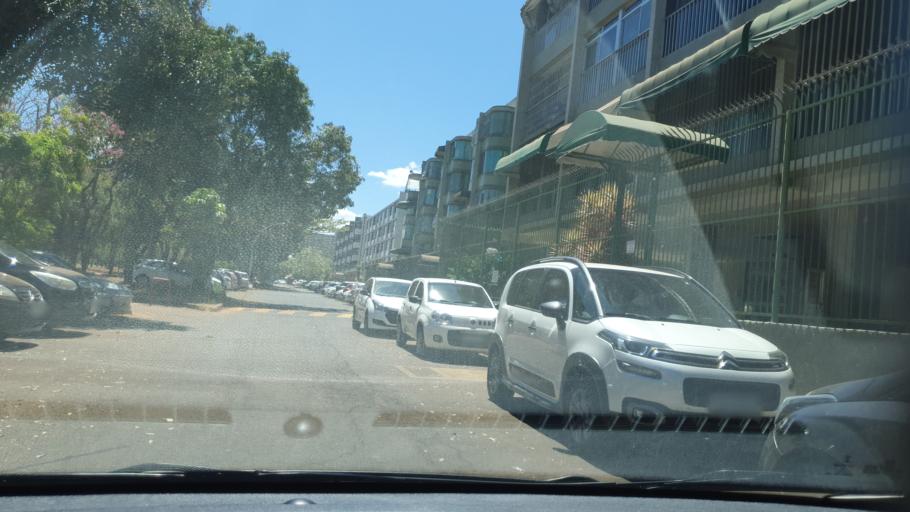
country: BR
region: Federal District
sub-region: Brasilia
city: Brasilia
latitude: -15.7978
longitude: -47.9444
